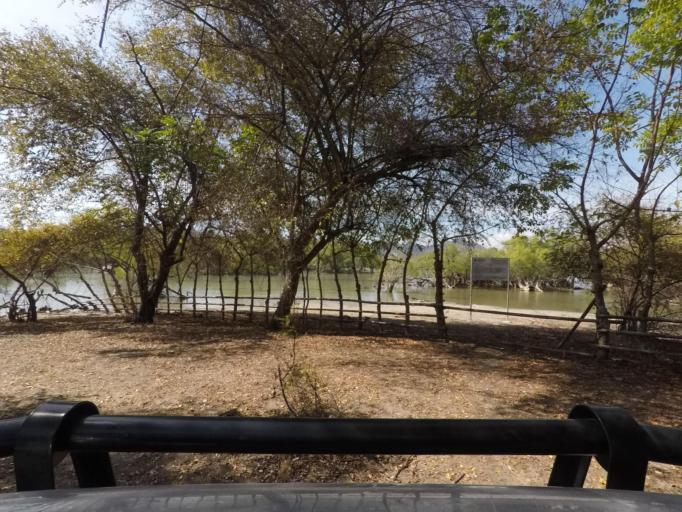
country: TL
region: Bobonaro
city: Maliana
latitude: -8.8767
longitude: 125.0100
